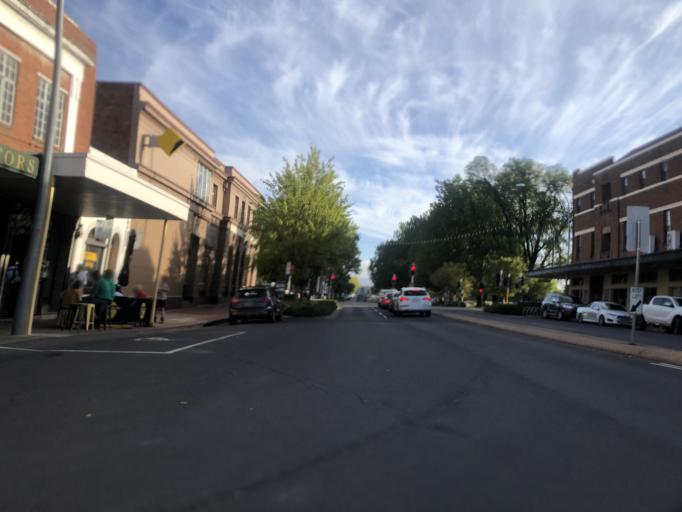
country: AU
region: New South Wales
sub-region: Orange Municipality
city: Orange
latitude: -33.2845
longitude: 149.1009
